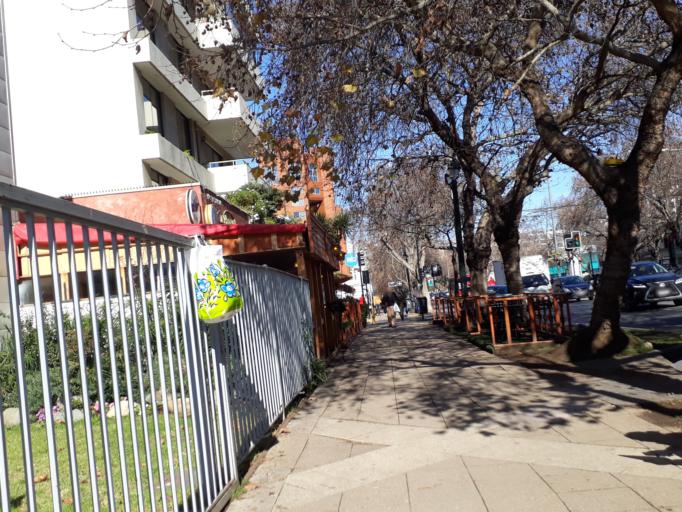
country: CL
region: Valparaiso
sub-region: Provincia de Valparaiso
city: Vina del Mar
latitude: -33.0128
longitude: -71.5494
